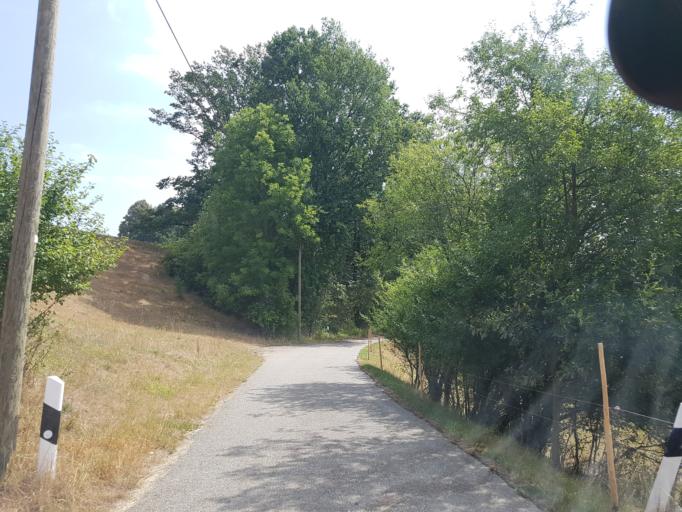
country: DE
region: Saxony
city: Waldheim
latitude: 51.0644
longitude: 13.0024
